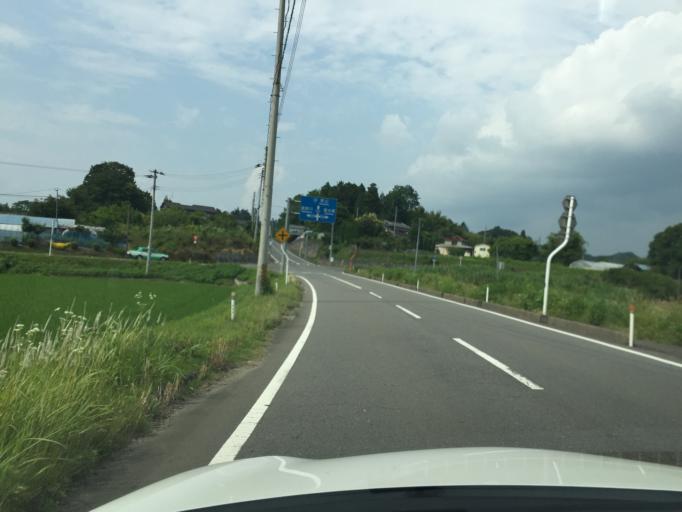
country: JP
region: Fukushima
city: Sukagawa
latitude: 37.2862
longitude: 140.4266
